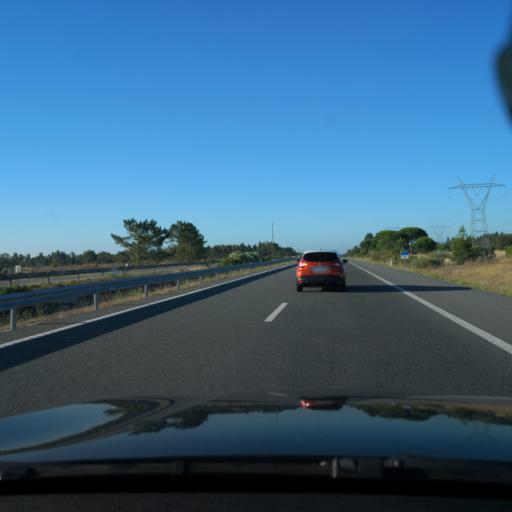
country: PT
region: Setubal
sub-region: Alcacer do Sal
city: Alcacer do Sal
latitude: 38.3083
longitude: -8.5085
